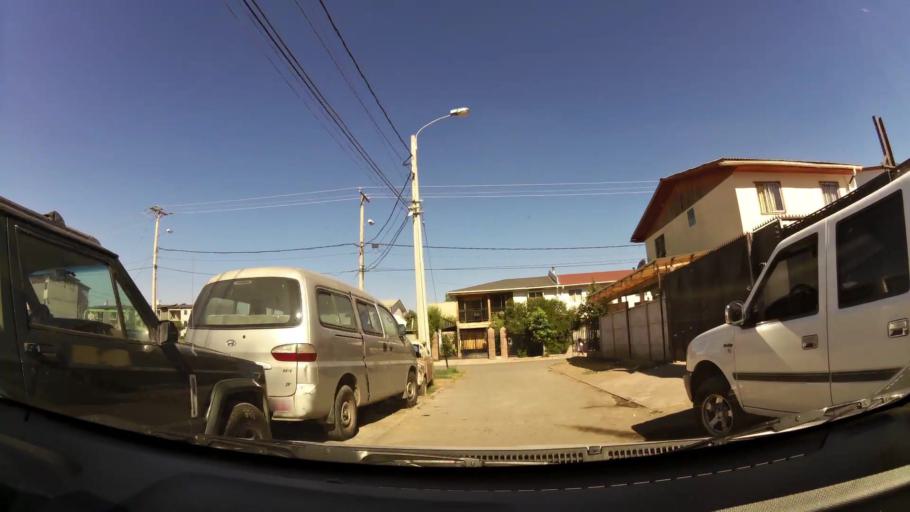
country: CL
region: O'Higgins
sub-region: Provincia de Colchagua
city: Chimbarongo
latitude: -34.5743
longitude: -71.0068
